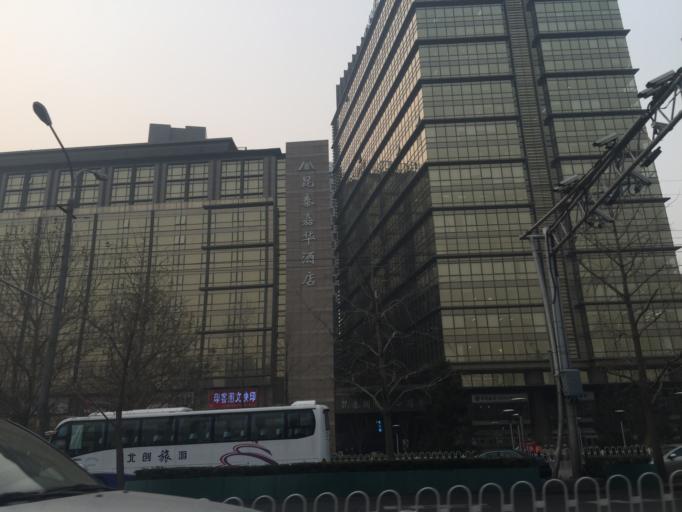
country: CN
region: Beijing
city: Chaowai
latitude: 39.9226
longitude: 116.4359
